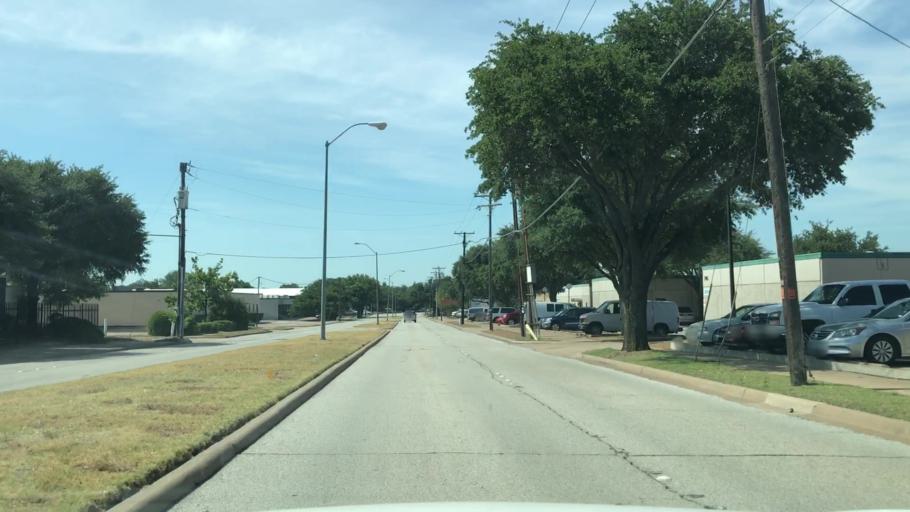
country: US
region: Texas
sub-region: Dallas County
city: Richardson
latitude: 32.9564
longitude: -96.7139
